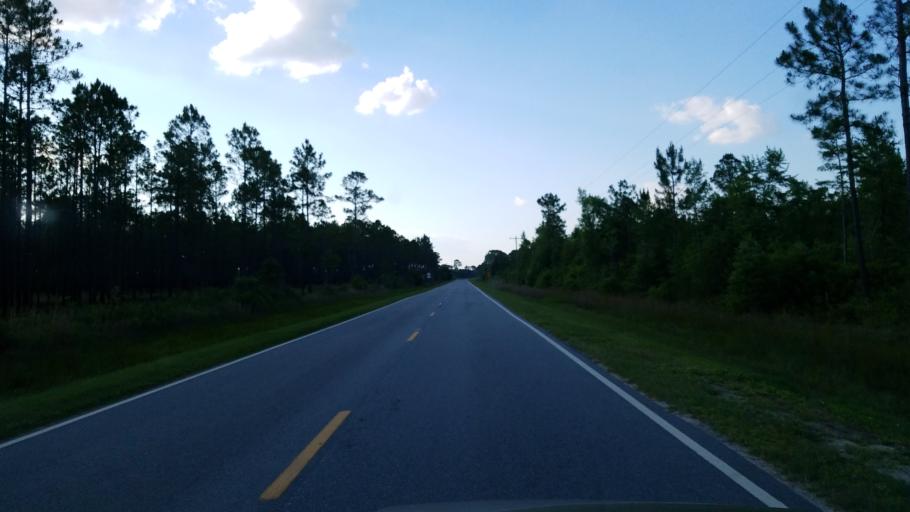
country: US
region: Georgia
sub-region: Lanier County
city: Lakeland
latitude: 31.1234
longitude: -83.0842
